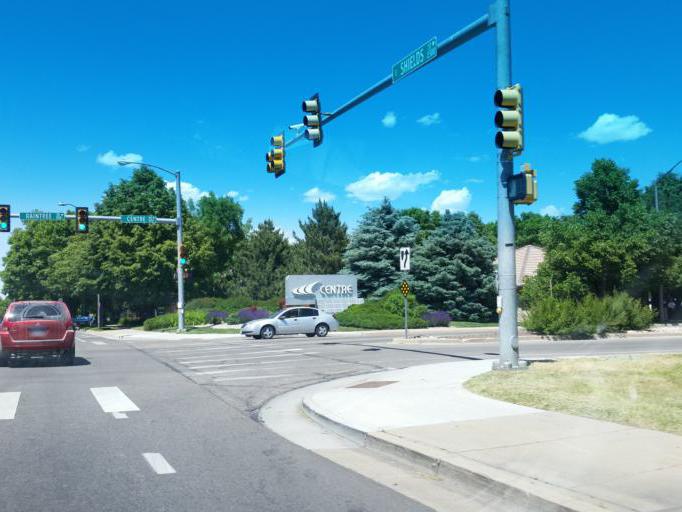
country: US
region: Colorado
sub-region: Larimer County
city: Fort Collins
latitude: 40.5552
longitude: -105.0960
